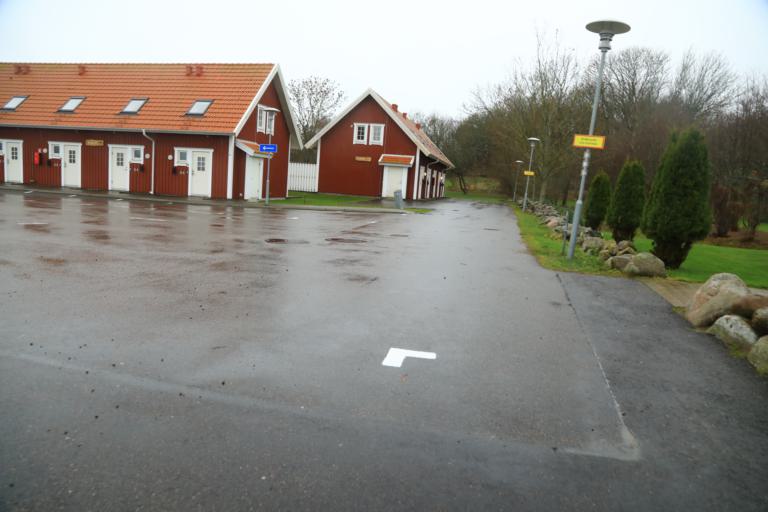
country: SE
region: Halland
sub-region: Varbergs Kommun
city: Varberg
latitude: 57.0864
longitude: 12.2474
